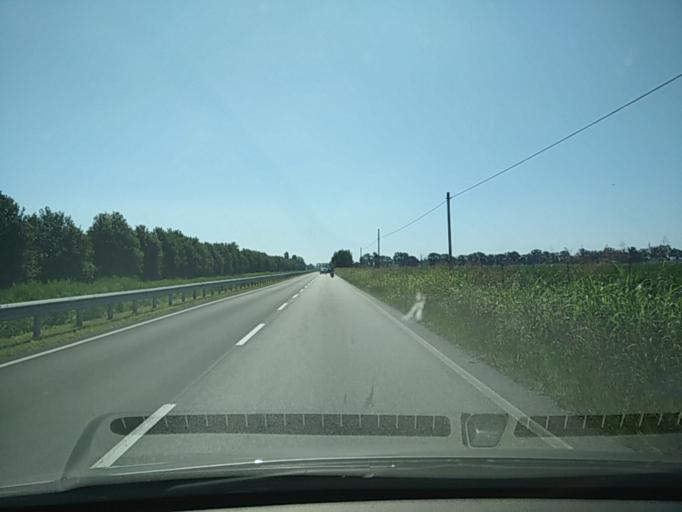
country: IT
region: Veneto
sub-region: Provincia di Venezia
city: San Giorgio di Livenza
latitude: 45.6268
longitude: 12.7854
